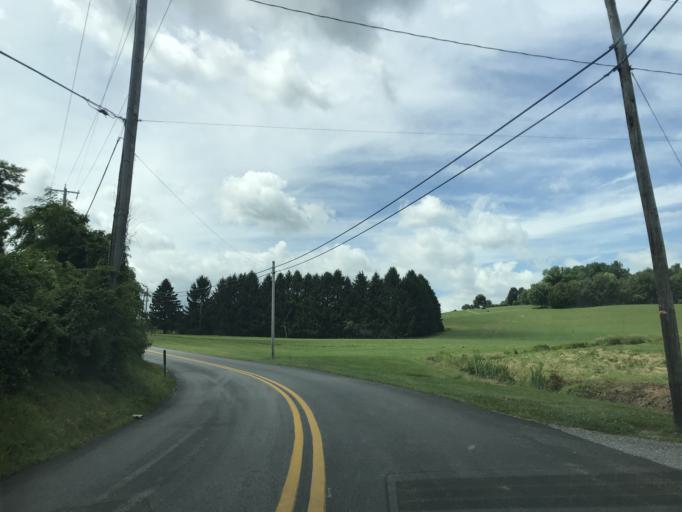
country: US
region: Maryland
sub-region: Carroll County
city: Hampstead
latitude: 39.6147
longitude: -76.7977
